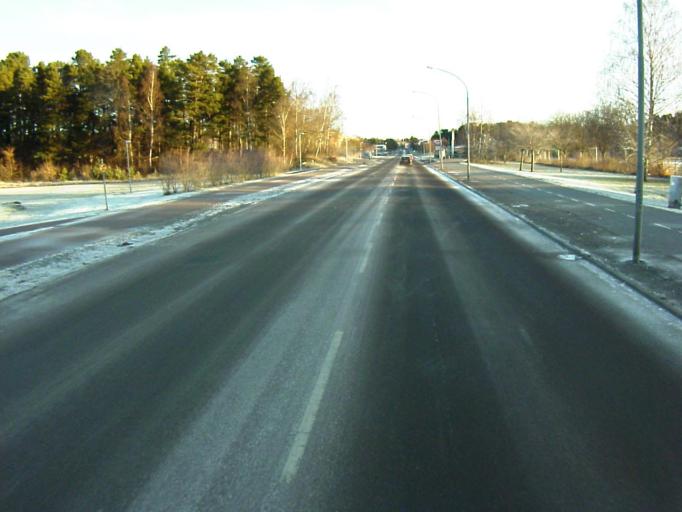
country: SE
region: Soedermanland
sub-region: Eskilstuna Kommun
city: Eskilstuna
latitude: 59.3552
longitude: 16.4858
